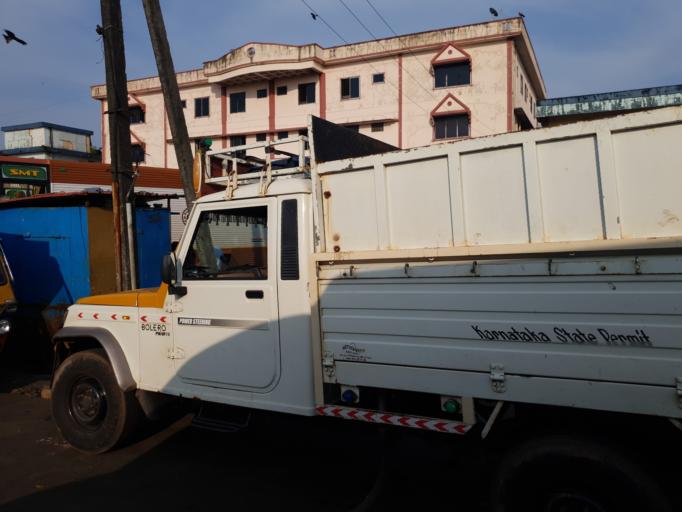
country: IN
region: Karnataka
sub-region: Dakshina Kannada
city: Ullal
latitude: 12.8542
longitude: 74.8335
